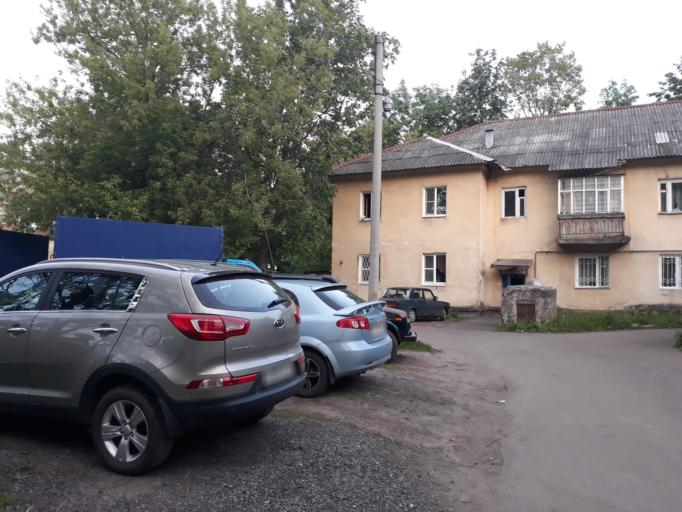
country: RU
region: Jaroslavl
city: Yaroslavl
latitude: 57.6412
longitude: 39.8309
